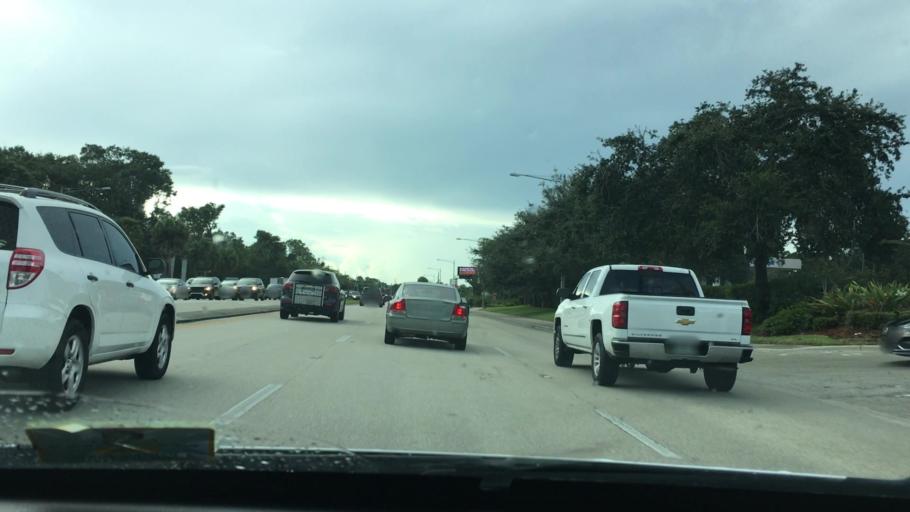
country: US
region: Florida
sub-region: Seminole County
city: Goldenrod
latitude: 28.5973
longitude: -81.2996
